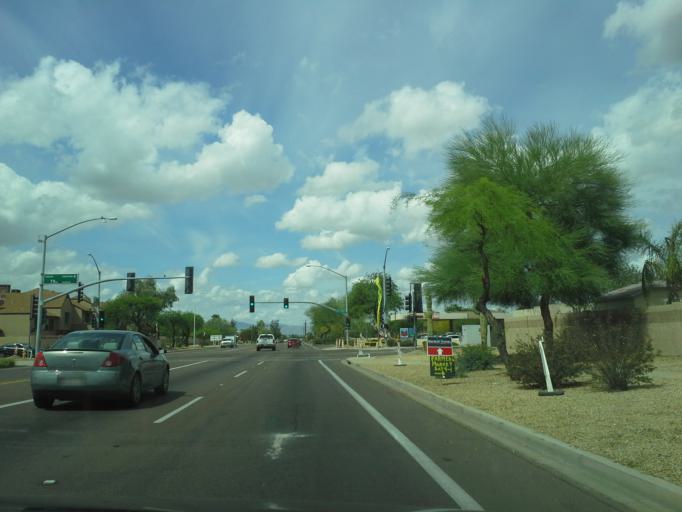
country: US
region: Arizona
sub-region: Maricopa County
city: Peoria
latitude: 33.6102
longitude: -112.2282
